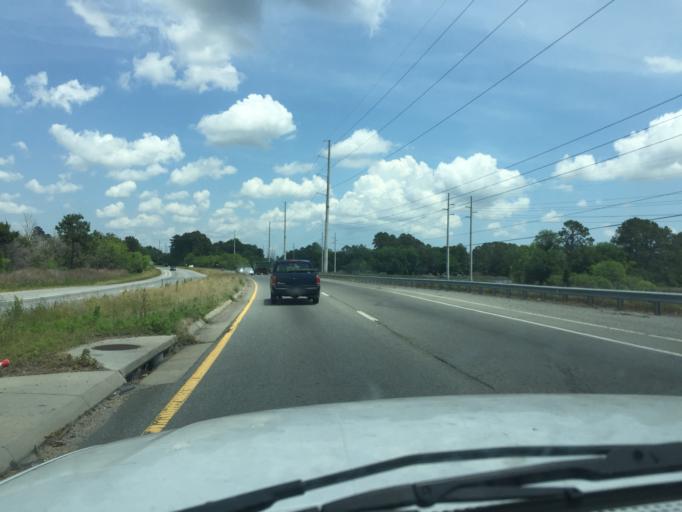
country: US
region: Georgia
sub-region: Chatham County
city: Georgetown
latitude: 32.0075
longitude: -81.2384
